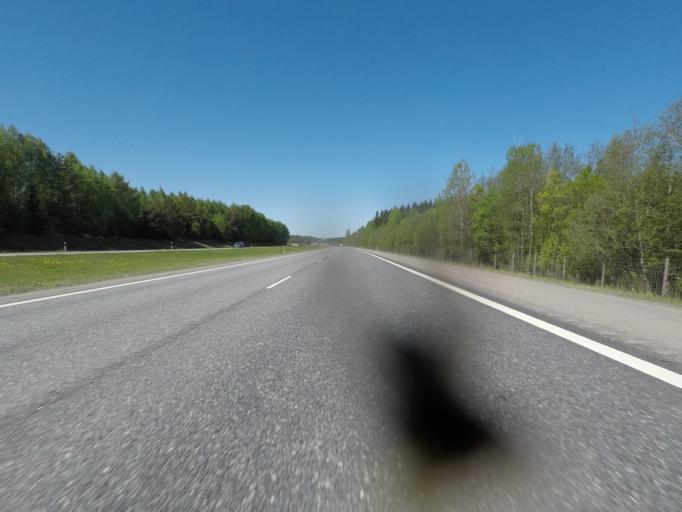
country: FI
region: Haeme
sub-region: Haemeenlinna
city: Tervakoski
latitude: 60.8391
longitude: 24.6421
